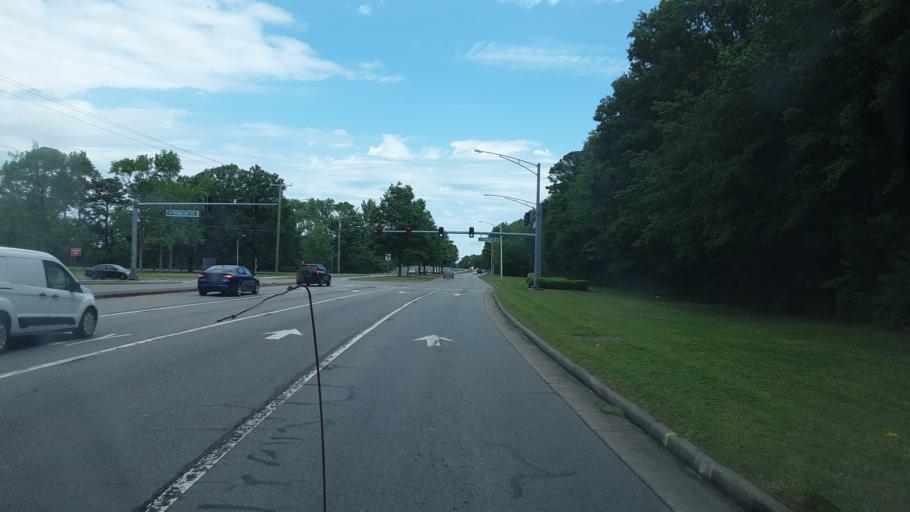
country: US
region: Virginia
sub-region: City of Virginia Beach
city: Virginia Beach
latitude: 36.8019
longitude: -76.0047
